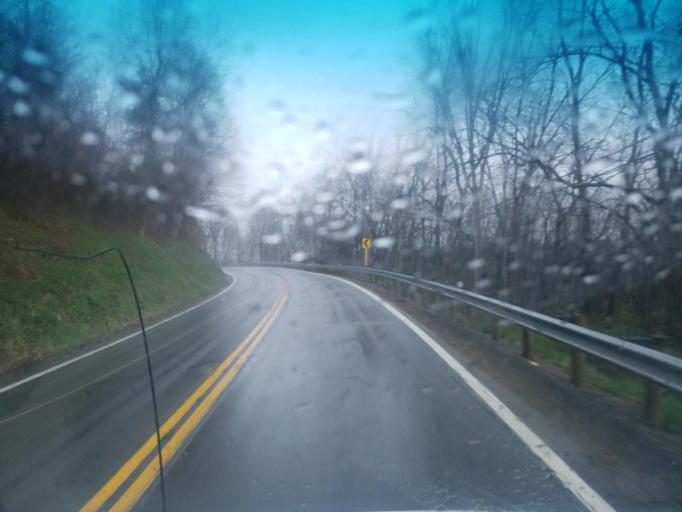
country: US
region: Ohio
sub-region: Holmes County
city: Millersburg
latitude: 40.4809
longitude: -82.0301
